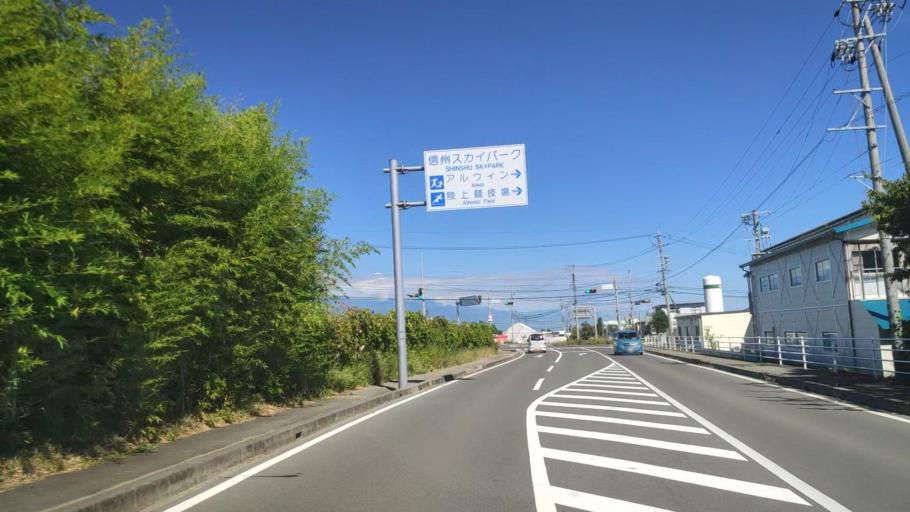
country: JP
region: Nagano
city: Matsumoto
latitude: 36.1690
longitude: 137.9160
